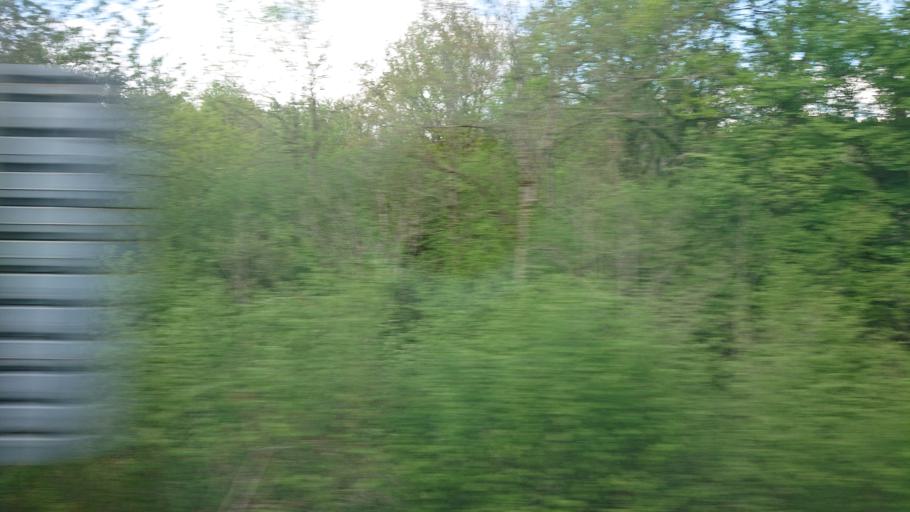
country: CH
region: Geneva
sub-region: Geneva
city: Chancy
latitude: 46.1341
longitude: 5.9433
